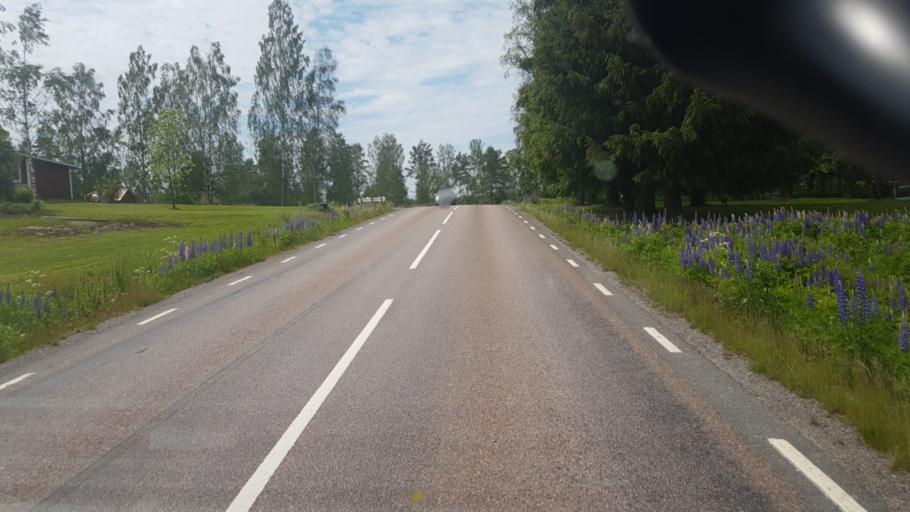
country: SE
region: Vaermland
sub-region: Eda Kommun
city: Charlottenberg
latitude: 59.8869
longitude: 12.3453
